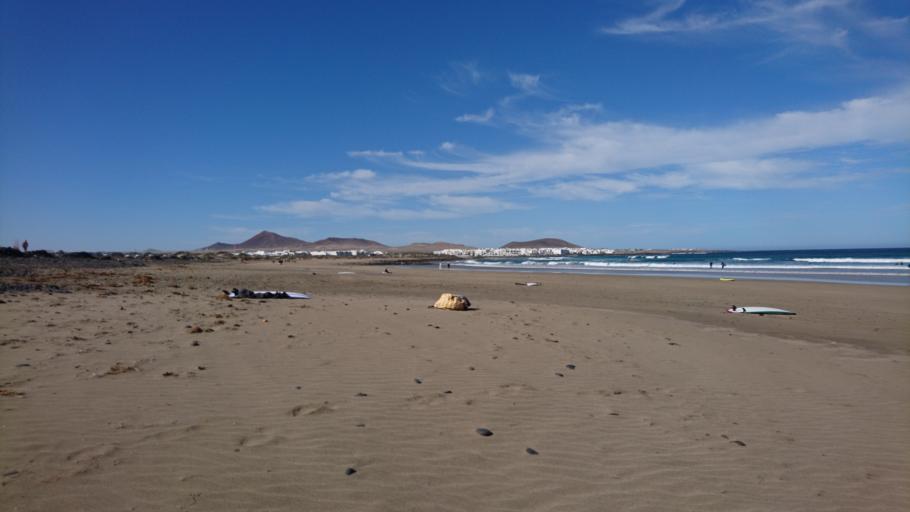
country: ES
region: Canary Islands
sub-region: Provincia de Las Palmas
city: Teguise
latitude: 29.1158
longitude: -13.5557
